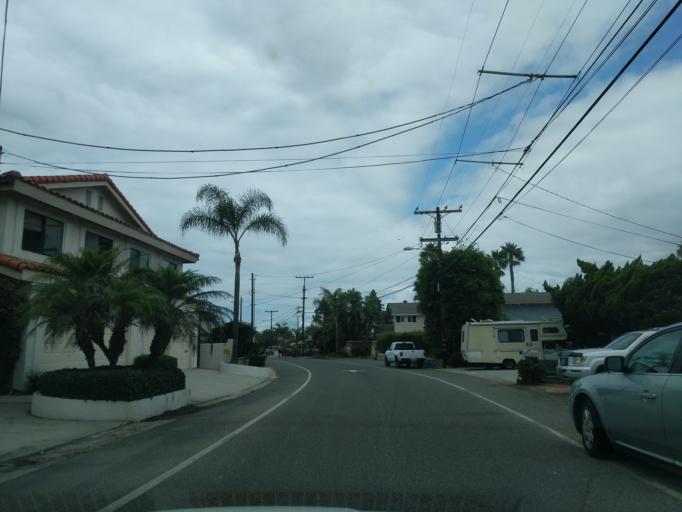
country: US
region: California
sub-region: San Diego County
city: Encinitas
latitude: 33.0661
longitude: -117.3049
